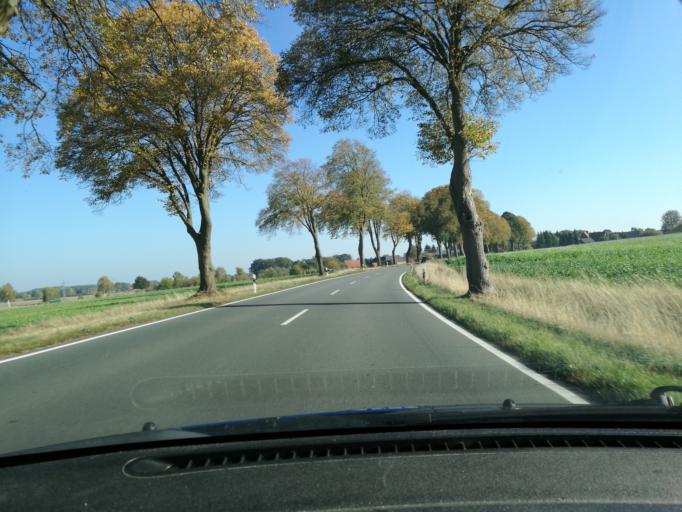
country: DE
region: Lower Saxony
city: Nahrendorf
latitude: 53.1611
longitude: 10.8047
